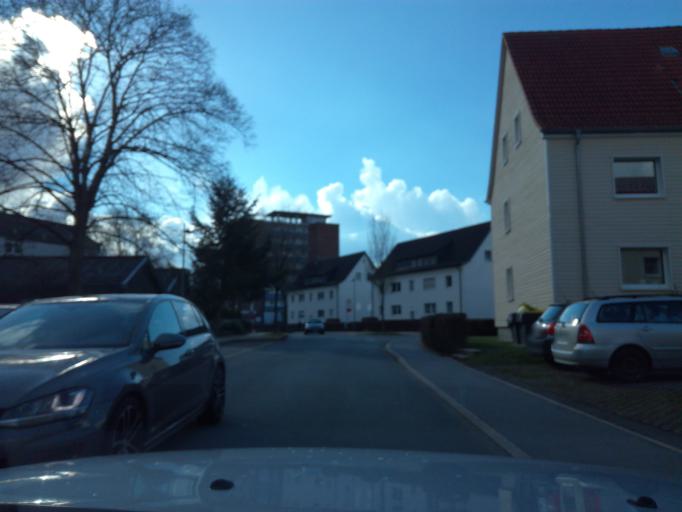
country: DE
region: North Rhine-Westphalia
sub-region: Regierungsbezirk Arnsberg
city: Menden
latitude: 51.4340
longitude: 7.7601
